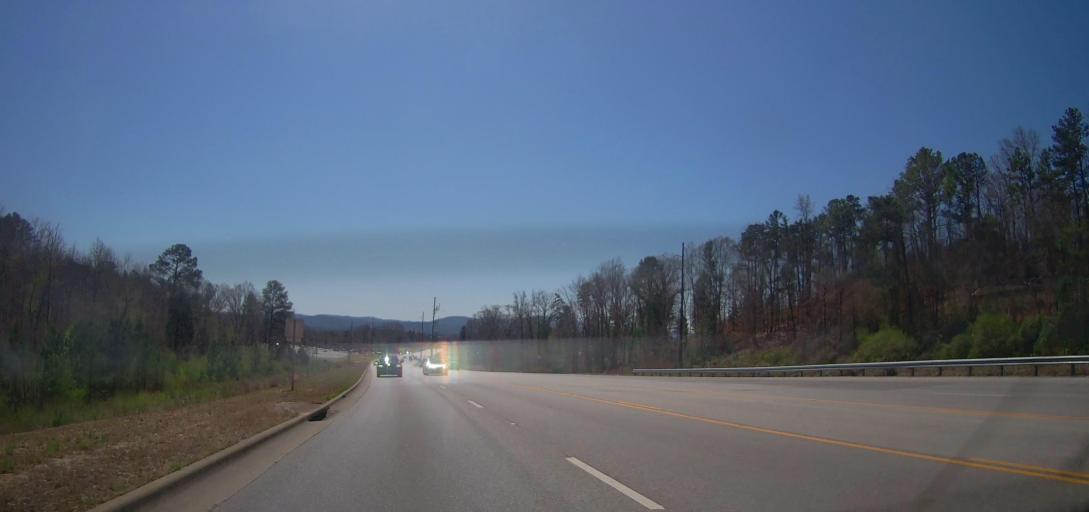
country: US
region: Alabama
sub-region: Calhoun County
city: Anniston
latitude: 33.6479
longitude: -85.7864
